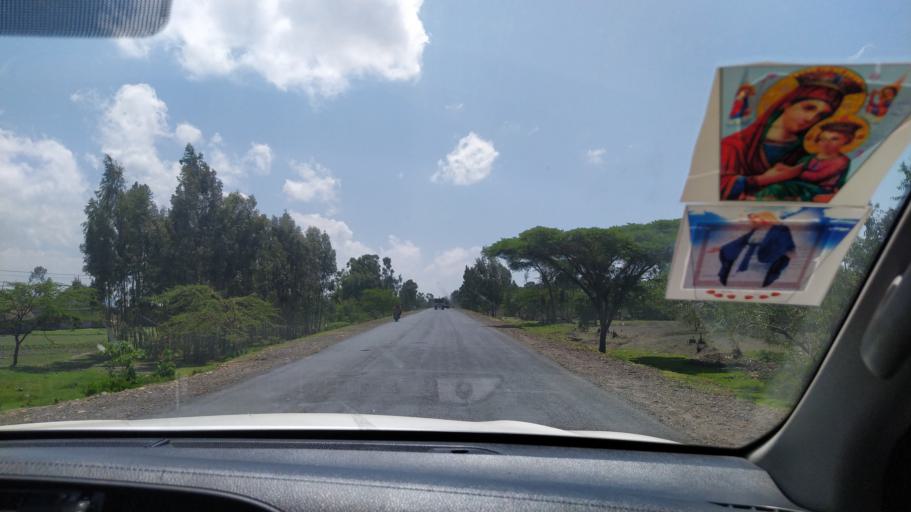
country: ET
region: Southern Nations, Nationalities, and People's Region
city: Butajira
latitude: 7.7590
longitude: 38.1324
